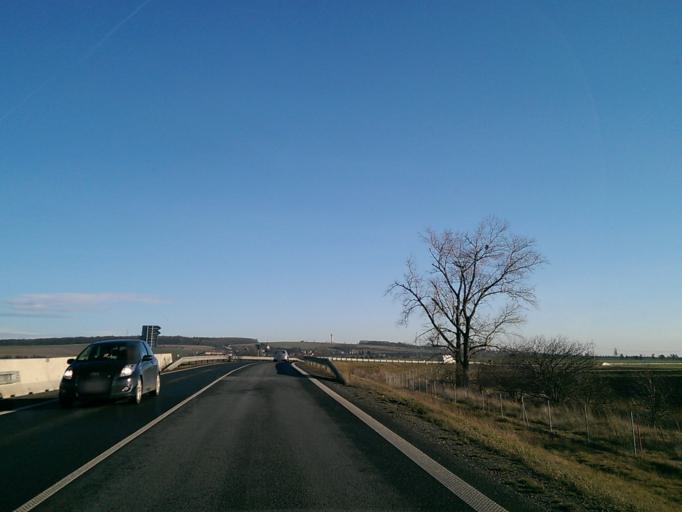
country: CZ
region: Olomoucky
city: Horni Mostenice
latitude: 49.3918
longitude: 17.4559
